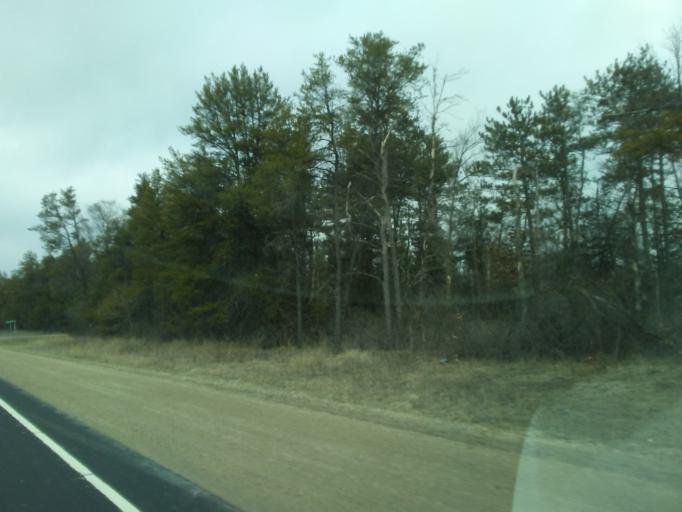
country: US
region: Wisconsin
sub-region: Richland County
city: Richland Center
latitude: 43.2156
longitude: -90.2831
